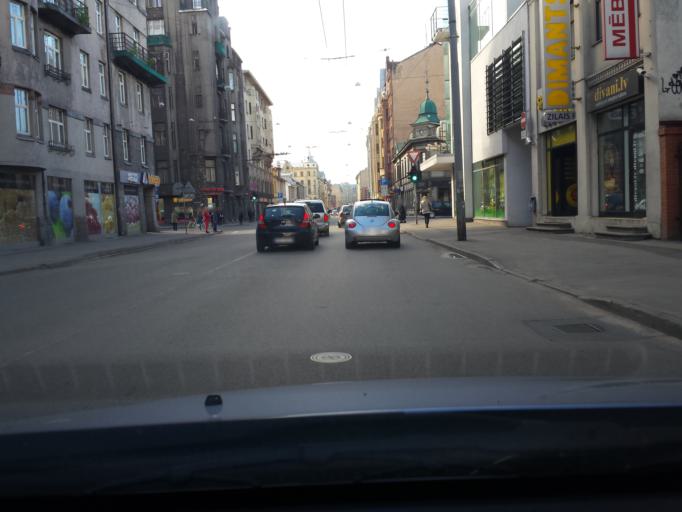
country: LV
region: Riga
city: Riga
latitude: 56.9557
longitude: 24.1364
